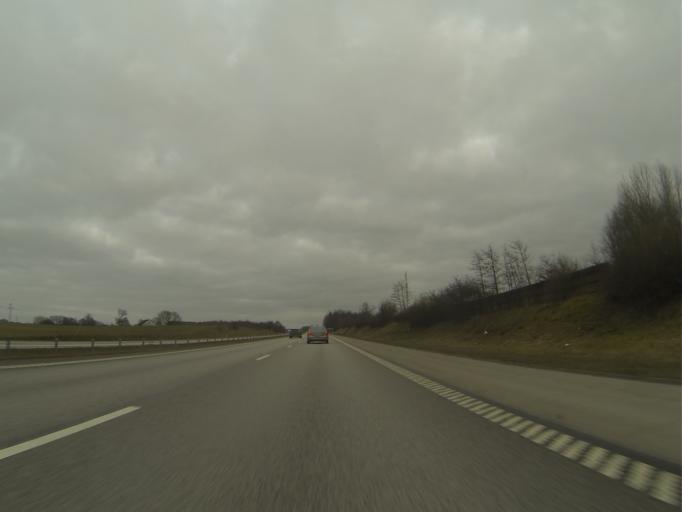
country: SE
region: Skane
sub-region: Svedala Kommun
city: Svedala
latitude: 55.5299
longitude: 13.1948
